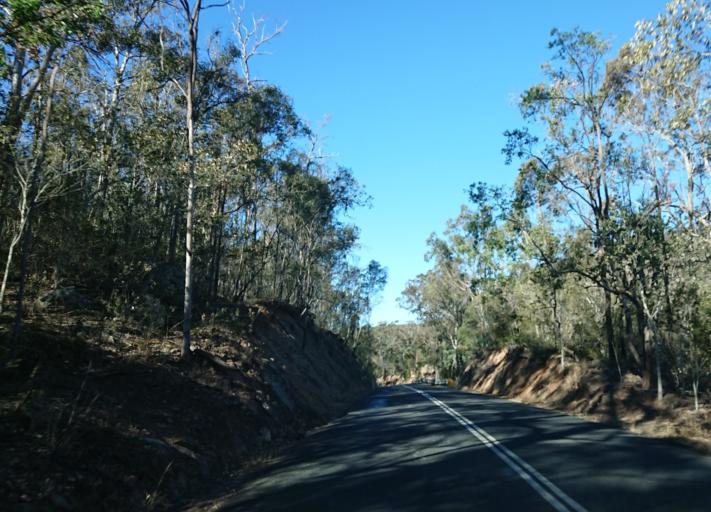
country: AU
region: Queensland
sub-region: Toowoomba
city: Top Camp
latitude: -27.7372
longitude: 152.1019
